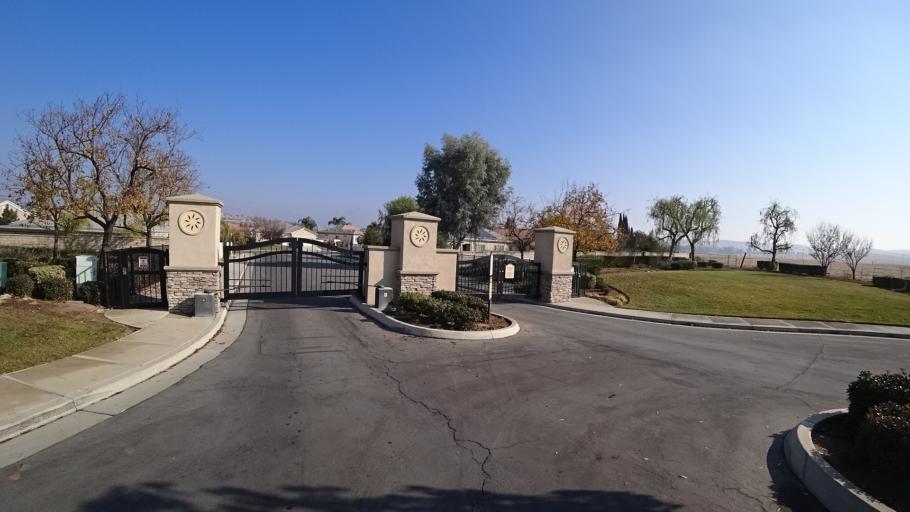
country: US
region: California
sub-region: Kern County
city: Lamont
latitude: 35.4057
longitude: -118.8570
